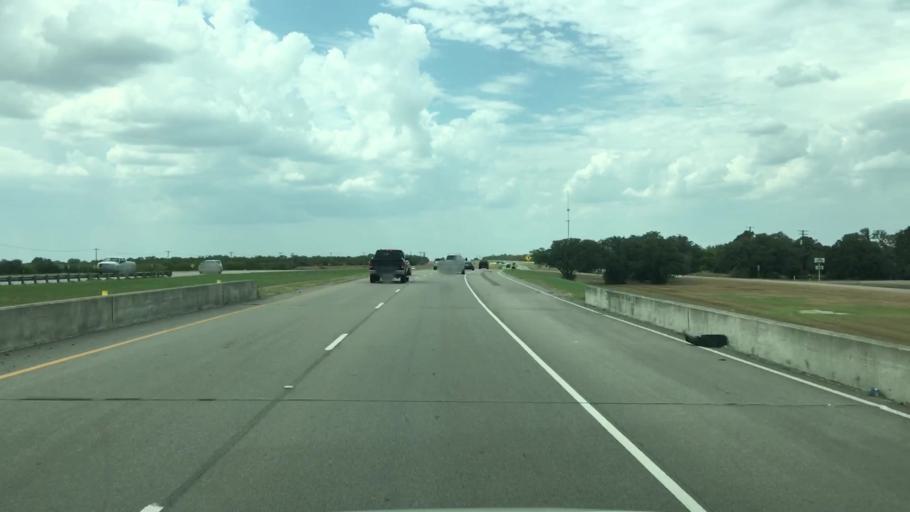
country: US
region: Texas
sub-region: Live Oak County
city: Three Rivers
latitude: 28.4894
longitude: -98.1431
